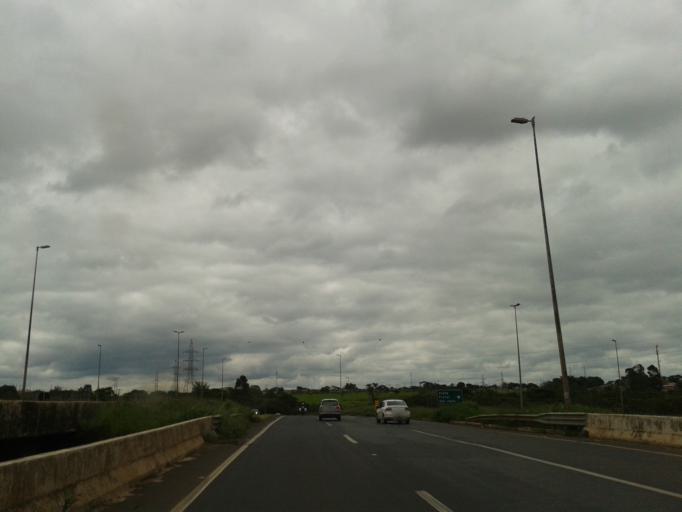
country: BR
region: Minas Gerais
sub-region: Uberlandia
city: Uberlandia
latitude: -18.9063
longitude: -48.3313
